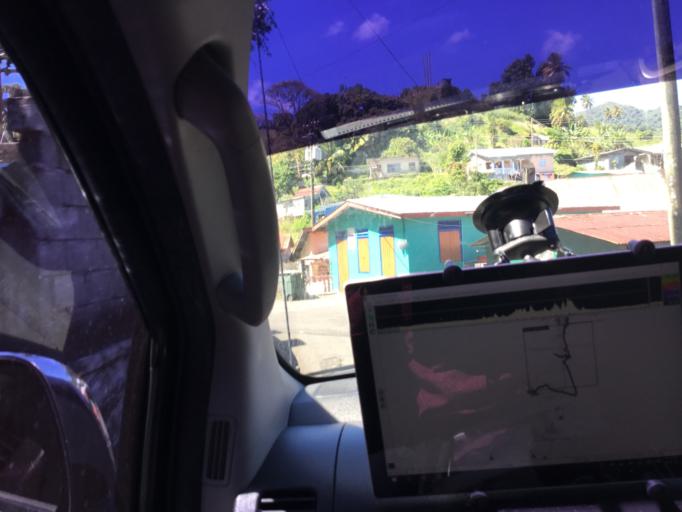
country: VC
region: Charlotte
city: Byera Village
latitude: 13.2443
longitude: -61.1404
